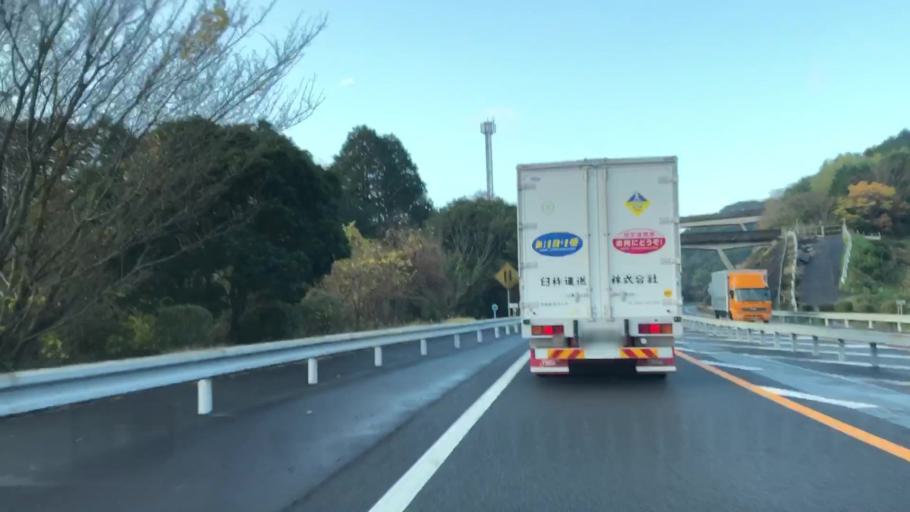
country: JP
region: Nagasaki
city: Sasebo
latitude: 33.1522
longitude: 129.8103
